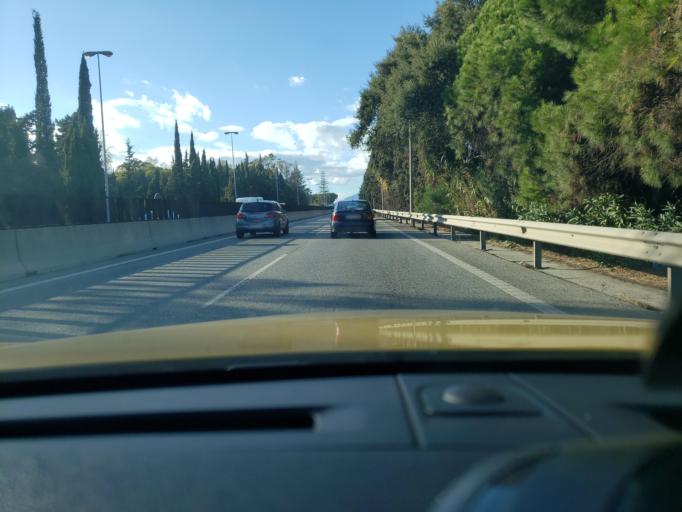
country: ES
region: Andalusia
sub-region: Provincia de Malaga
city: Ojen
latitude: 36.4977
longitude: -4.7878
